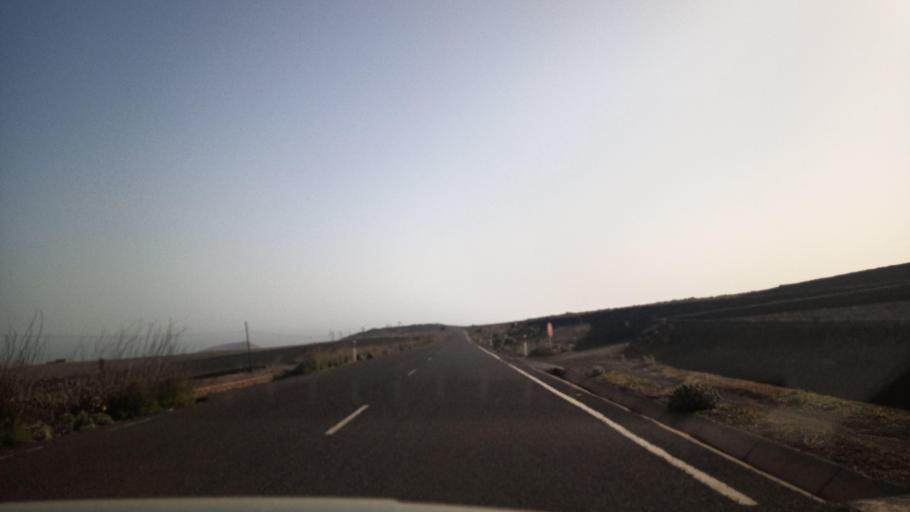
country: ES
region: Canary Islands
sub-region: Provincia de Las Palmas
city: Haria
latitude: 29.1191
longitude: -13.5152
